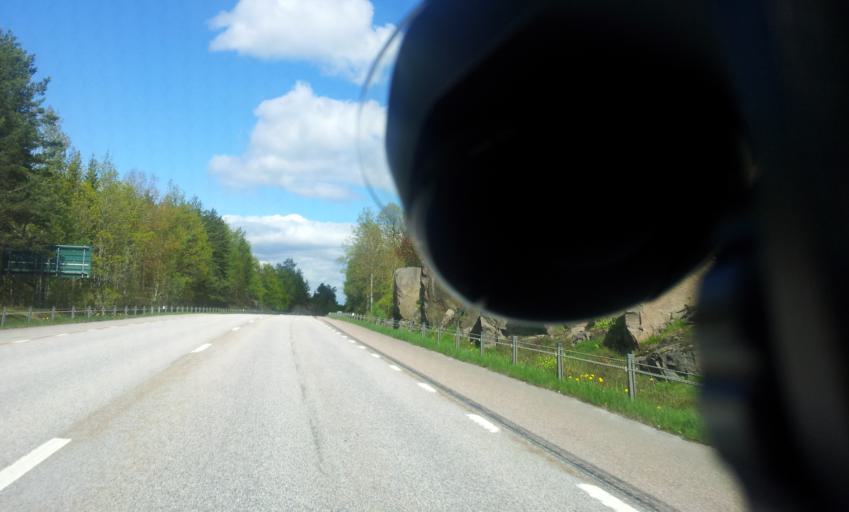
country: SE
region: Kalmar
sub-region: Vasterviks Kommun
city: Ankarsrum
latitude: 57.5629
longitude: 16.4777
